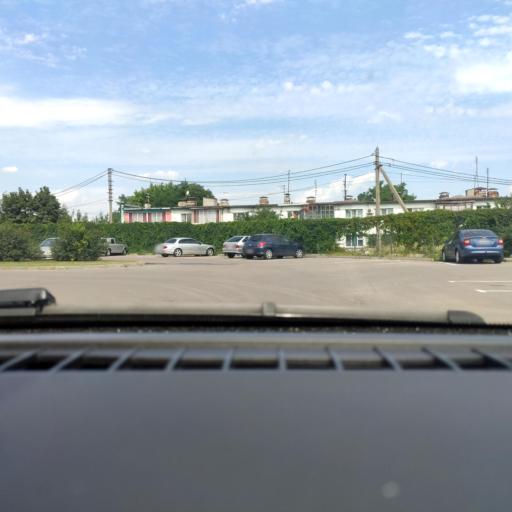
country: RU
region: Voronezj
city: Novaya Usman'
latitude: 51.6516
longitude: 39.3344
